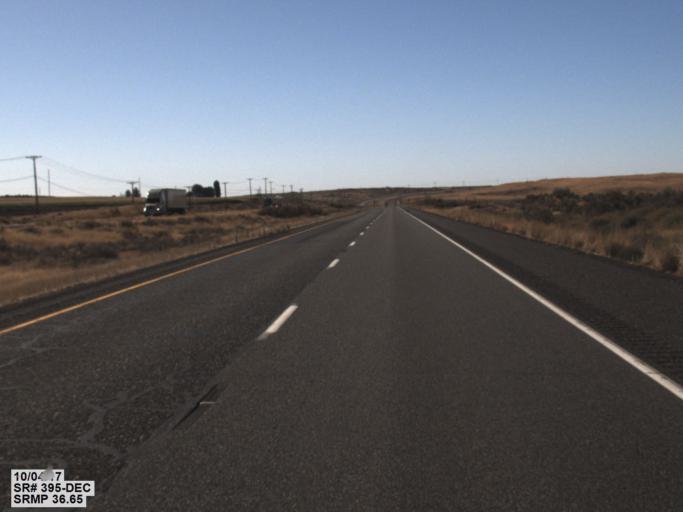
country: US
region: Washington
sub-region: Franklin County
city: Basin City
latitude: 46.4383
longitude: -119.0222
